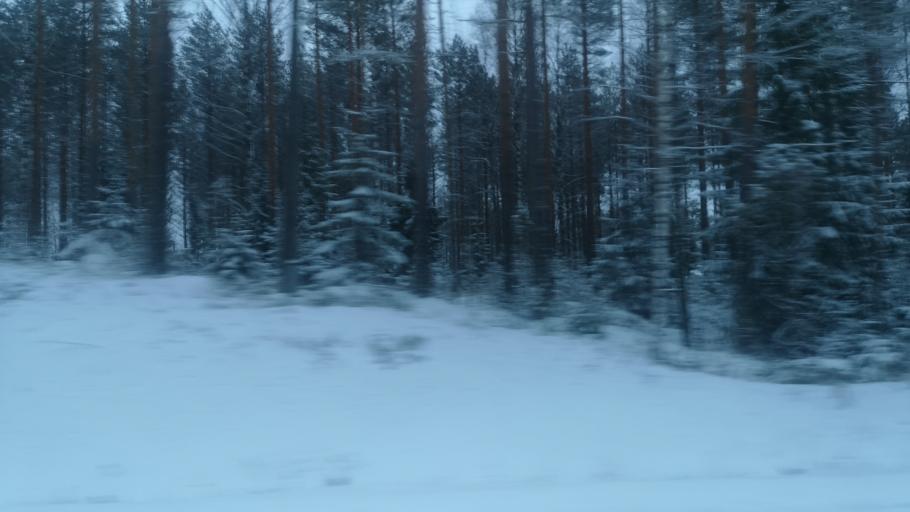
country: FI
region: Southern Savonia
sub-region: Savonlinna
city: Savonlinna
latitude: 62.0179
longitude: 28.7283
